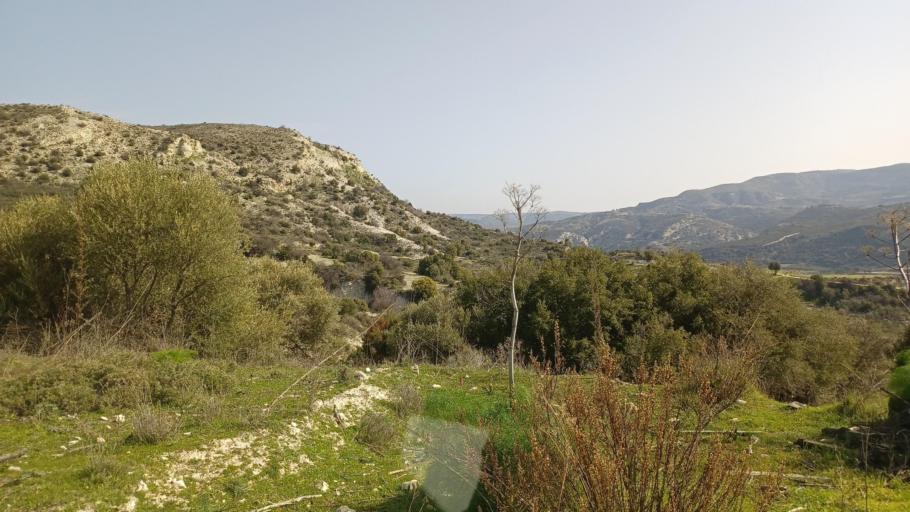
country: CY
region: Limassol
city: Pachna
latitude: 34.7980
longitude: 32.6940
